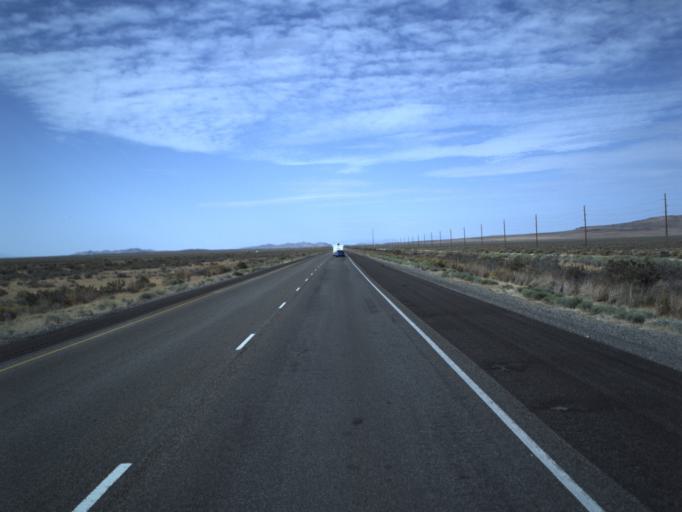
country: US
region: Utah
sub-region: Tooele County
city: Grantsville
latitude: 40.7480
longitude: -113.0573
